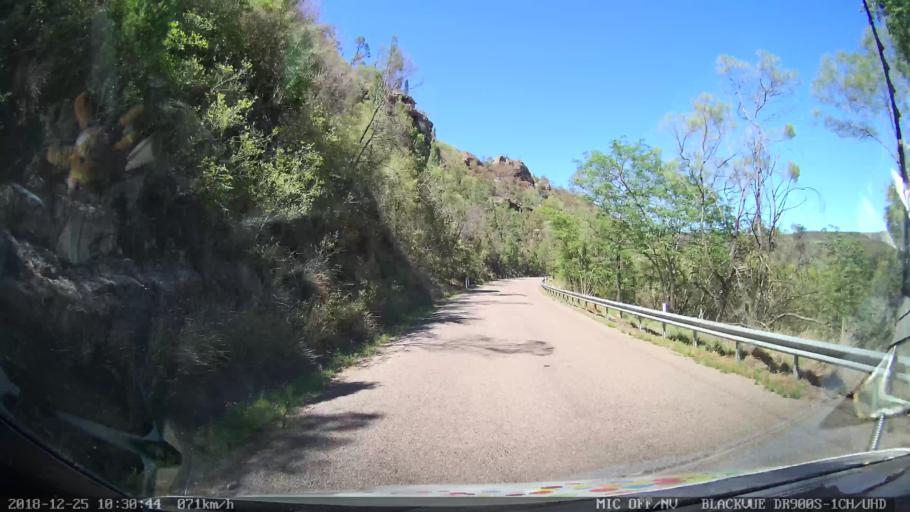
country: AU
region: New South Wales
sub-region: Muswellbrook
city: Denman
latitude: -32.3841
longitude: 150.4355
